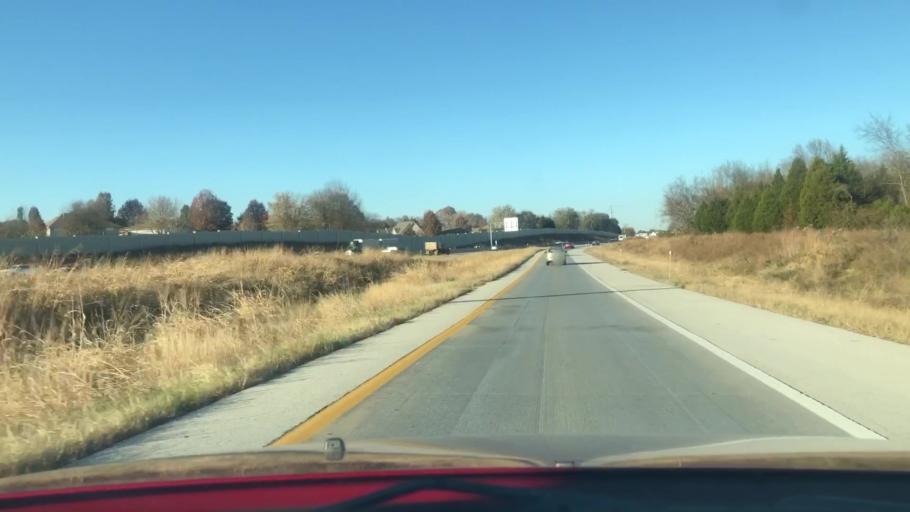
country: US
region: Missouri
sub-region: Greene County
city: Springfield
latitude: 37.1311
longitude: -93.2277
